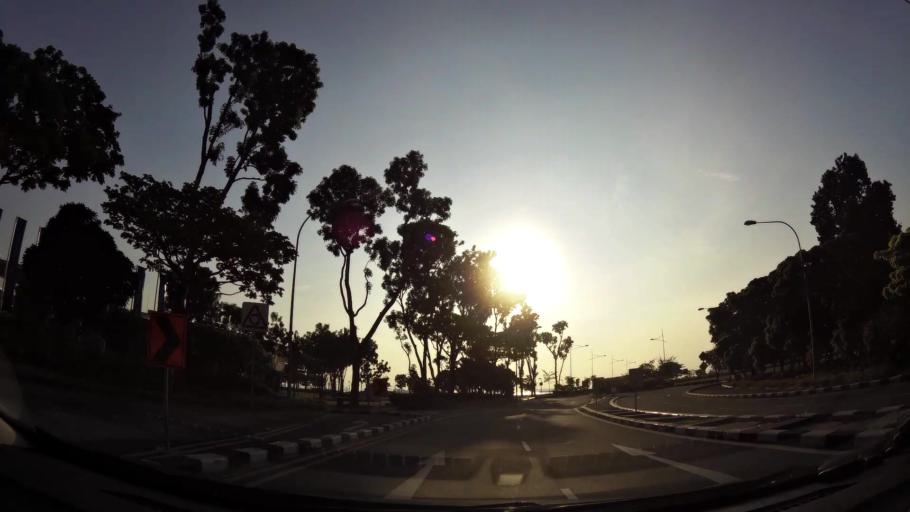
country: SG
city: Singapore
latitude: 1.2795
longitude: 103.8698
